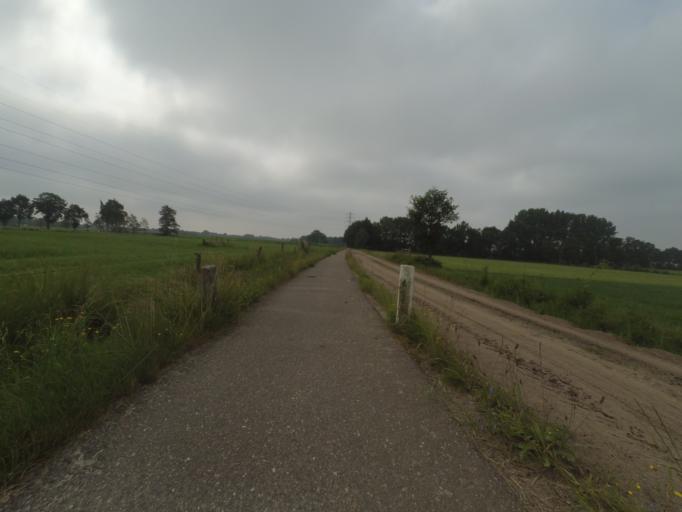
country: NL
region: Gelderland
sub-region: Gemeente Barneveld
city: Kootwijkerbroek
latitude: 52.1184
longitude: 5.6589
